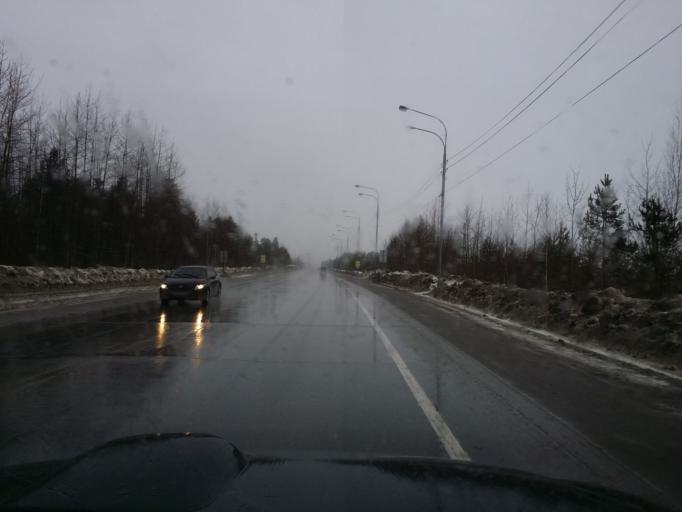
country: RU
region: Khanty-Mansiyskiy Avtonomnyy Okrug
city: Izluchinsk
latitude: 60.9656
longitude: 76.8404
